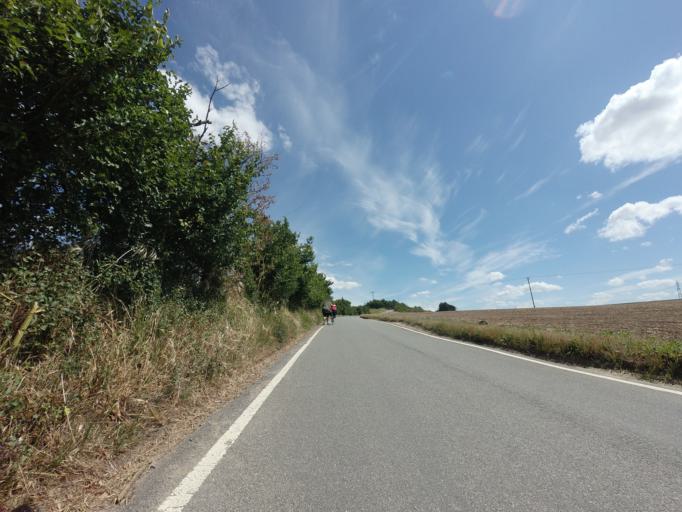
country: GB
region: England
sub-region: Medway
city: High Halstow
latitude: 51.4516
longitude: 0.5475
